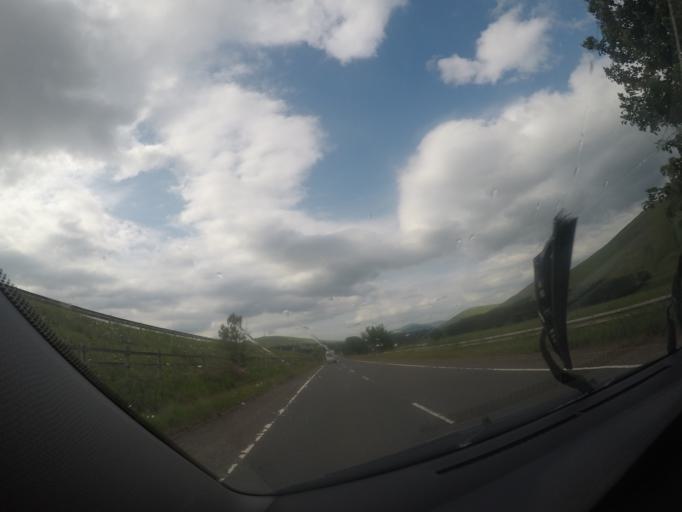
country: GB
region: Scotland
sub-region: South Lanarkshire
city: Douglas
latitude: 55.4766
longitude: -3.6952
